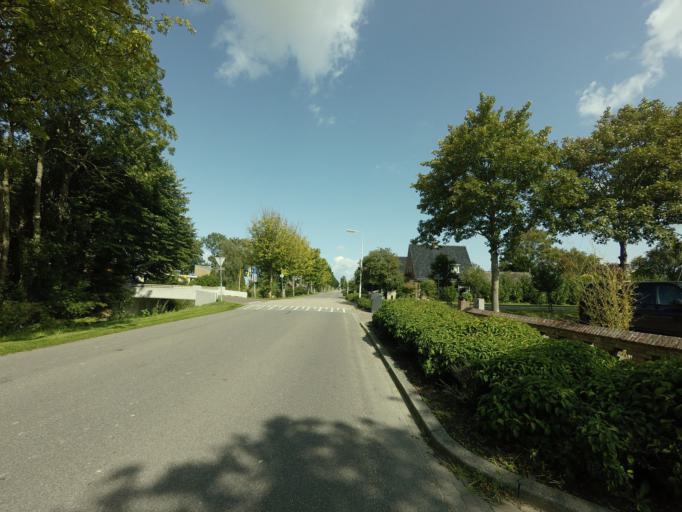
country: NL
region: Friesland
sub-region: Gemeente Het Bildt
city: Sint Annaparochie
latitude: 53.2806
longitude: 5.6563
